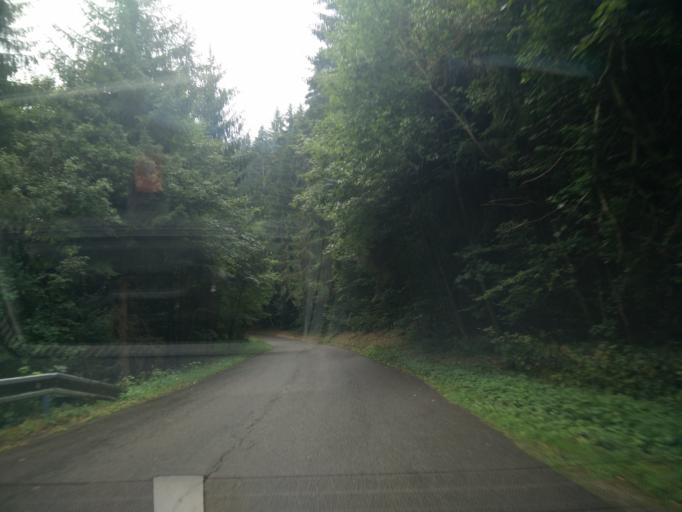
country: SK
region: Banskobystricky
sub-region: Okres Banska Bystrica
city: Banska Stiavnica
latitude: 48.4930
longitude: 18.8437
